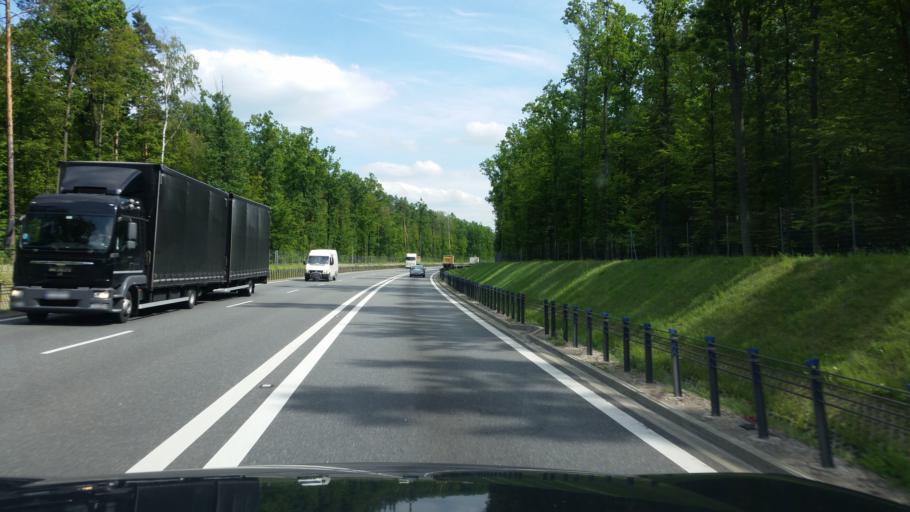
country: PL
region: Masovian Voivodeship
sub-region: Powiat zyrardowski
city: Wiskitki
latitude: 52.0611
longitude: 20.3987
